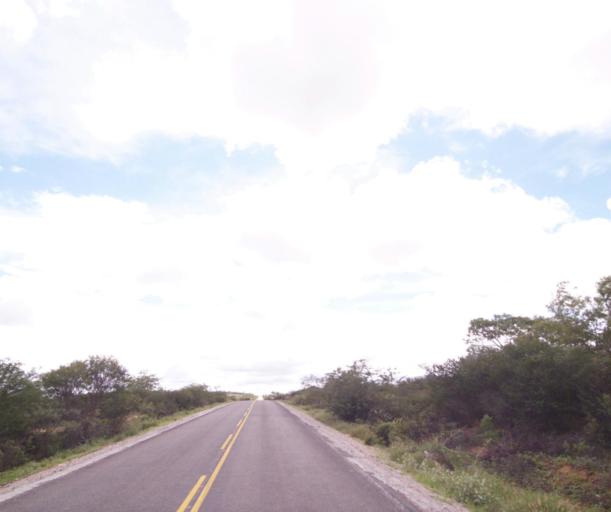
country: BR
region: Bahia
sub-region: Tanhacu
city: Tanhacu
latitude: -14.1575
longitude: -41.2514
